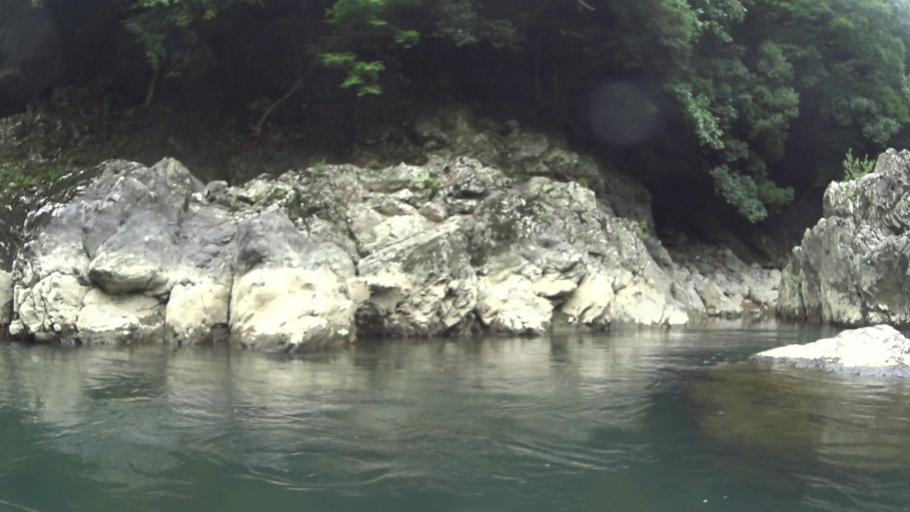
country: JP
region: Kyoto
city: Kameoka
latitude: 35.0207
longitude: 135.6223
